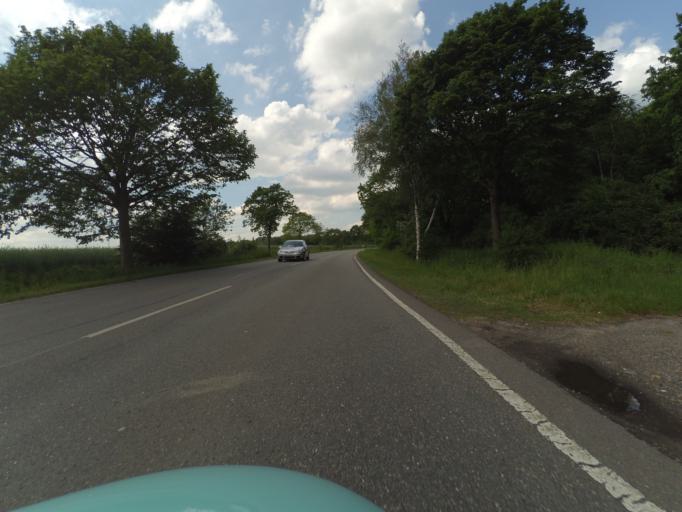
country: DE
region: Lower Saxony
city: Lehrte
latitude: 52.3811
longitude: 10.0171
